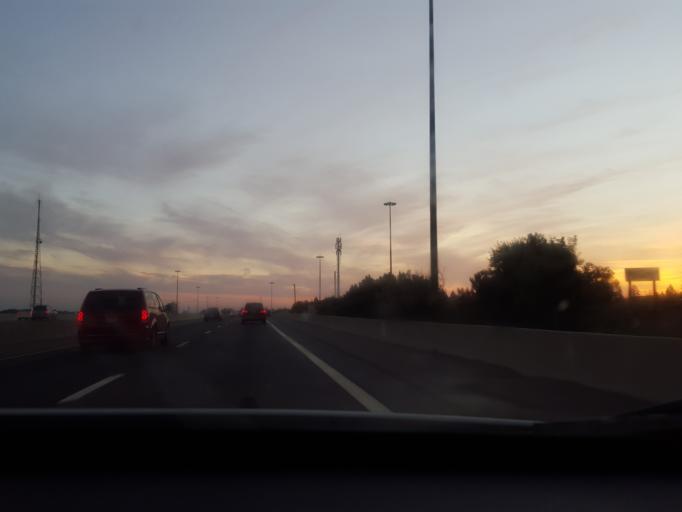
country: CA
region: Ontario
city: Willowdale
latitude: 43.7558
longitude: -79.4054
